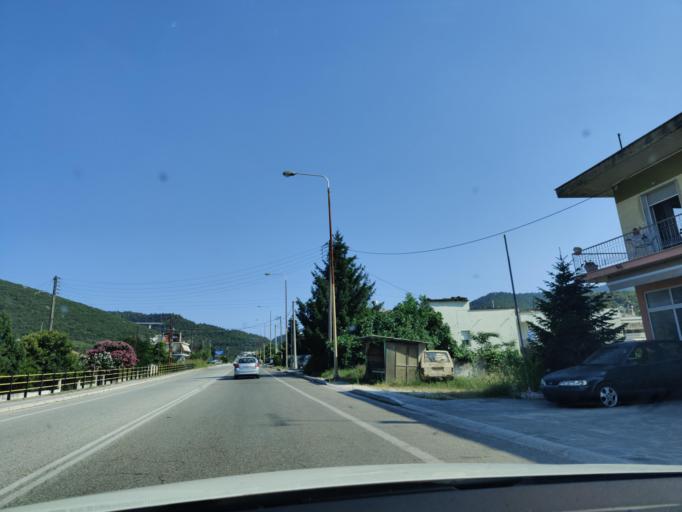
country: GR
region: East Macedonia and Thrace
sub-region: Nomos Kavalas
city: Amygdaleonas
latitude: 40.9599
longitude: 24.3617
